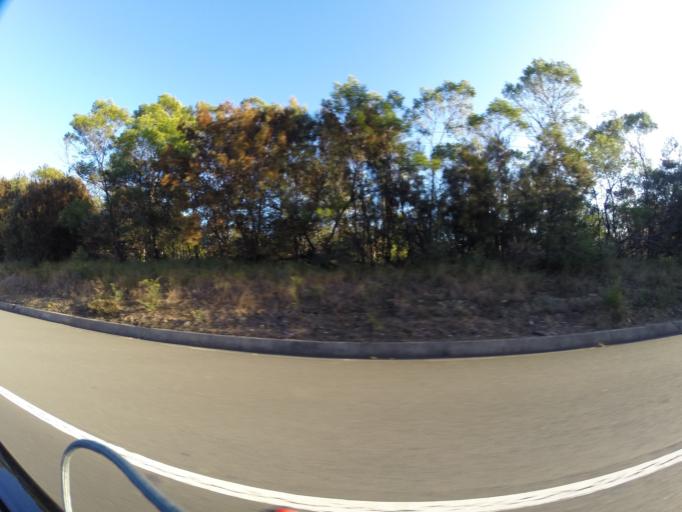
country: AU
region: New South Wales
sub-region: Sutherland Shire
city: Loftus
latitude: -34.0535
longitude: 151.0472
